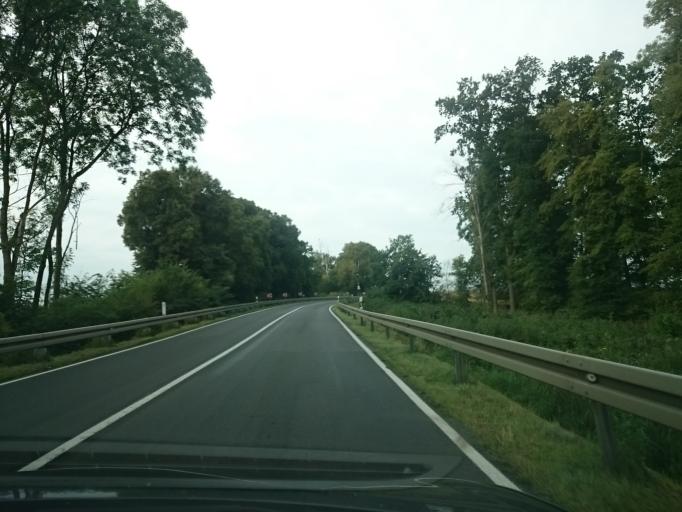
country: DE
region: Mecklenburg-Vorpommern
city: Mollenhagen
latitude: 53.5348
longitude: 12.8266
